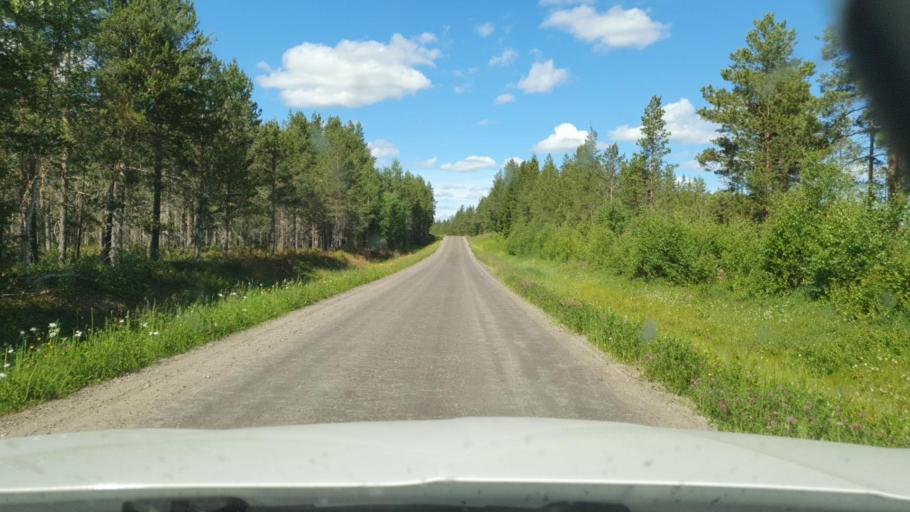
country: SE
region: Vaesterbotten
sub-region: Skelleftea Kommun
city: Byske
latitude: 65.1377
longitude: 21.1861
